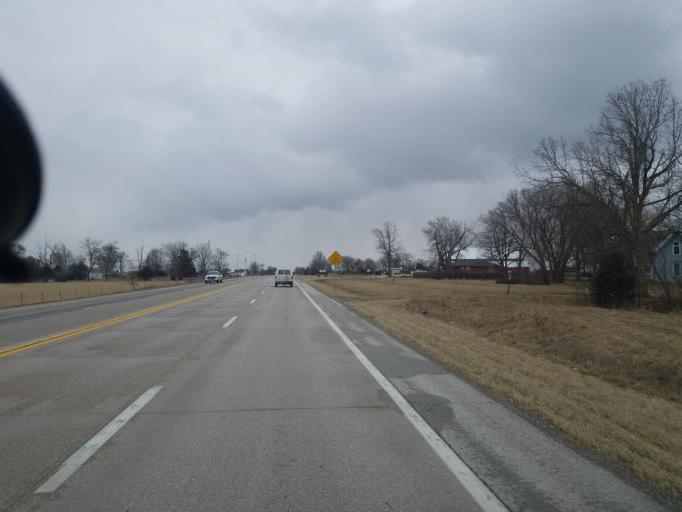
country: US
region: Missouri
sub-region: Macon County
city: Macon
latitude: 39.7783
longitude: -92.4780
